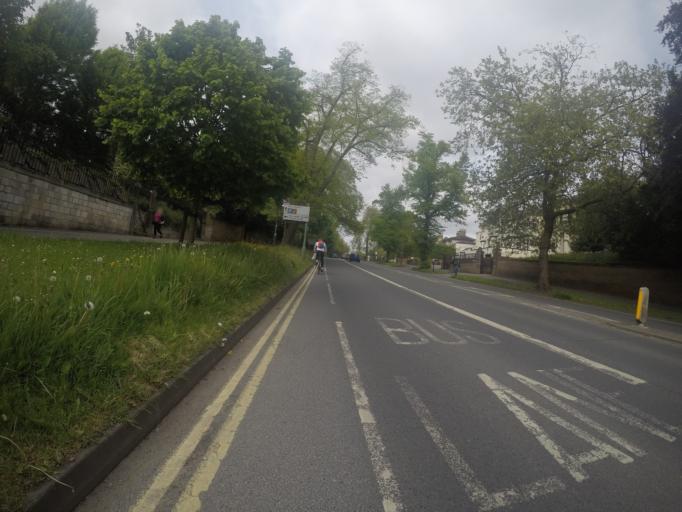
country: GB
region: England
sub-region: City of York
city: York
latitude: 53.9510
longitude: -1.0979
